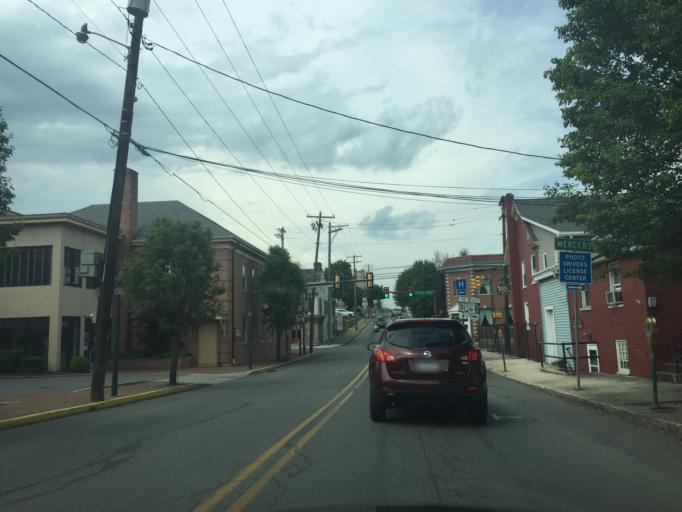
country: US
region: Pennsylvania
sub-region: Fulton County
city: McConnellsburg
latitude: 39.9321
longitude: -77.9994
